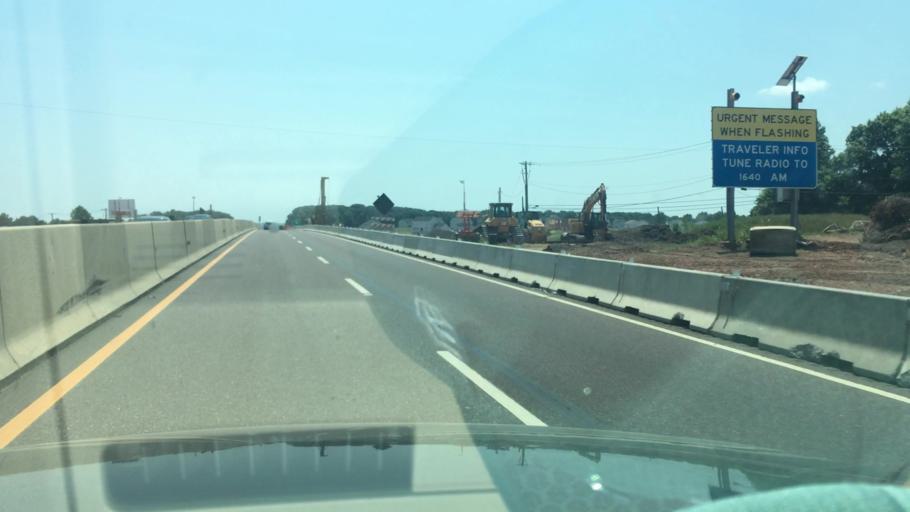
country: US
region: Pennsylvania
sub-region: Montgomery County
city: Harleysville
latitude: 40.2903
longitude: -75.3656
